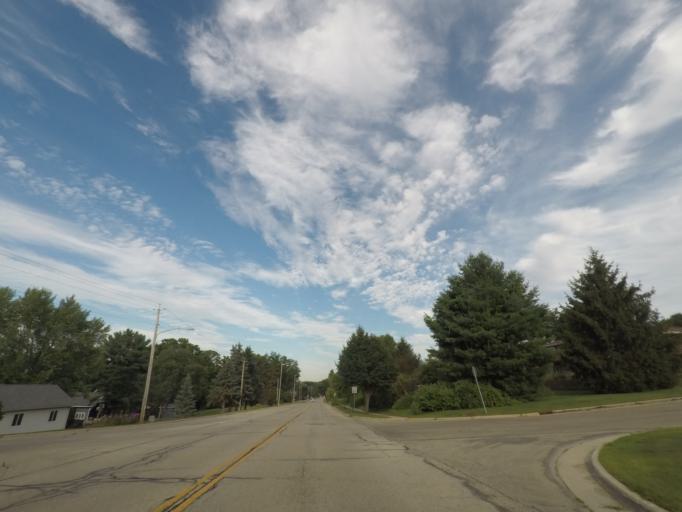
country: US
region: Wisconsin
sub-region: Green County
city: New Glarus
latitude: 42.8145
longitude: -89.6451
